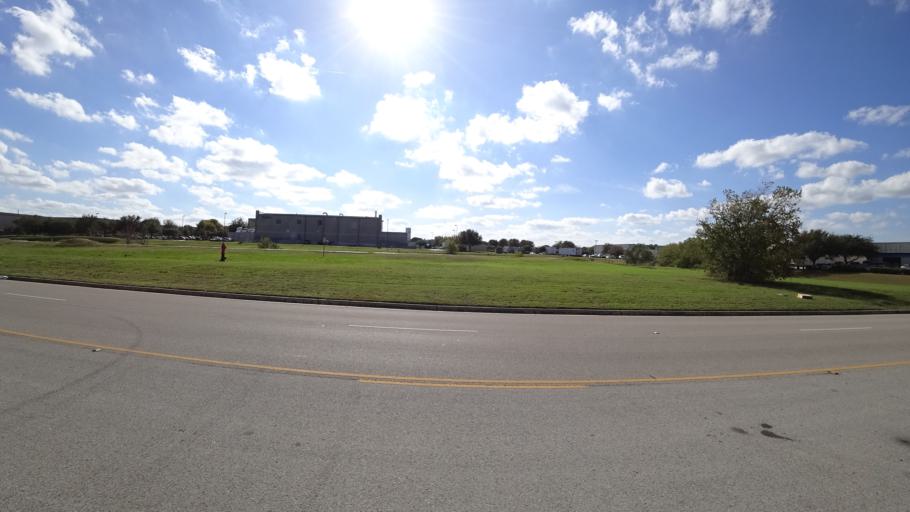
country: US
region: Texas
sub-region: Travis County
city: Wells Branch
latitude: 30.4746
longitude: -97.6749
